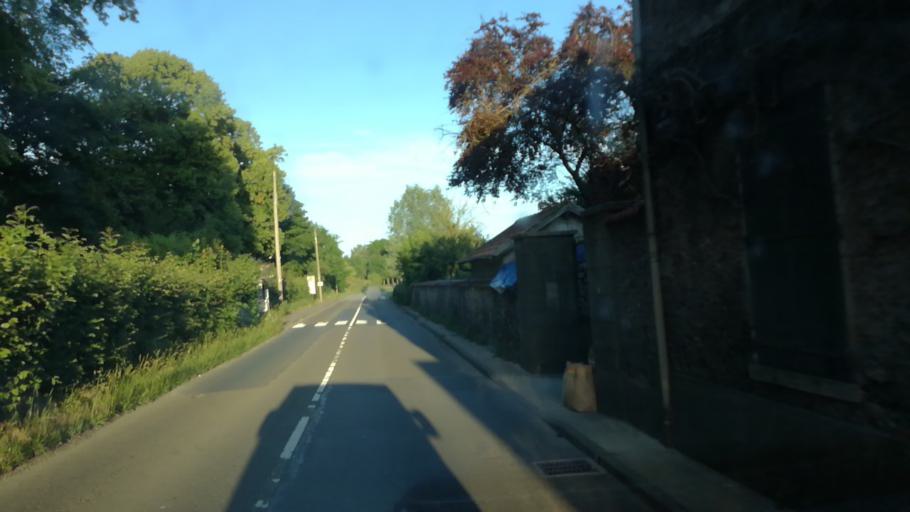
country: FR
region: Ile-de-France
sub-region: Departement des Yvelines
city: Le Mesnil-Saint-Denis
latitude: 48.7419
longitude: 1.9661
